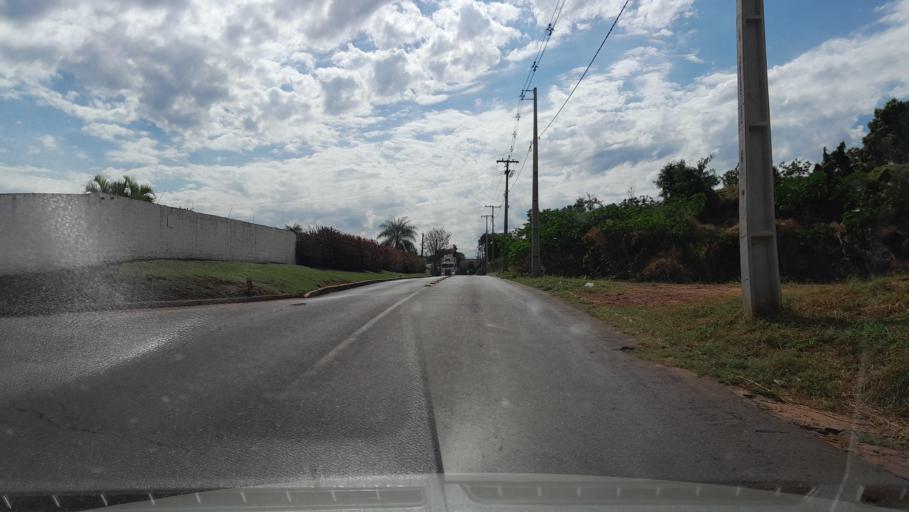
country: BR
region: Parana
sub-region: Umuarama
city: Umuarama
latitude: -23.7778
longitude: -53.2996
